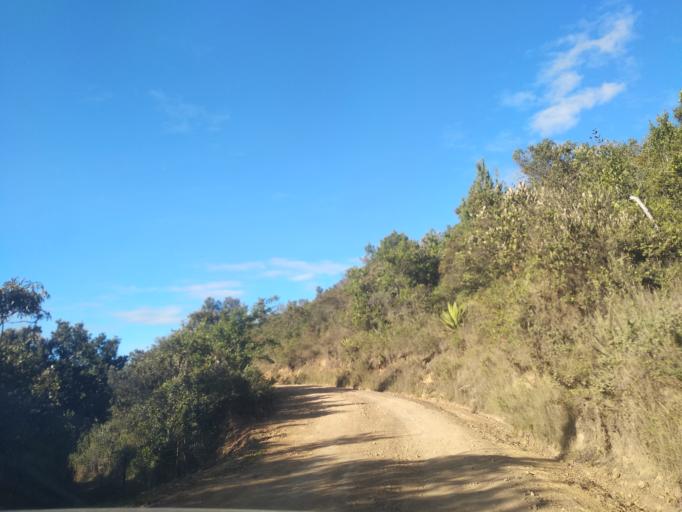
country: CO
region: Boyaca
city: Santa Rosa de Viterbo
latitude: 5.8630
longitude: -72.9735
